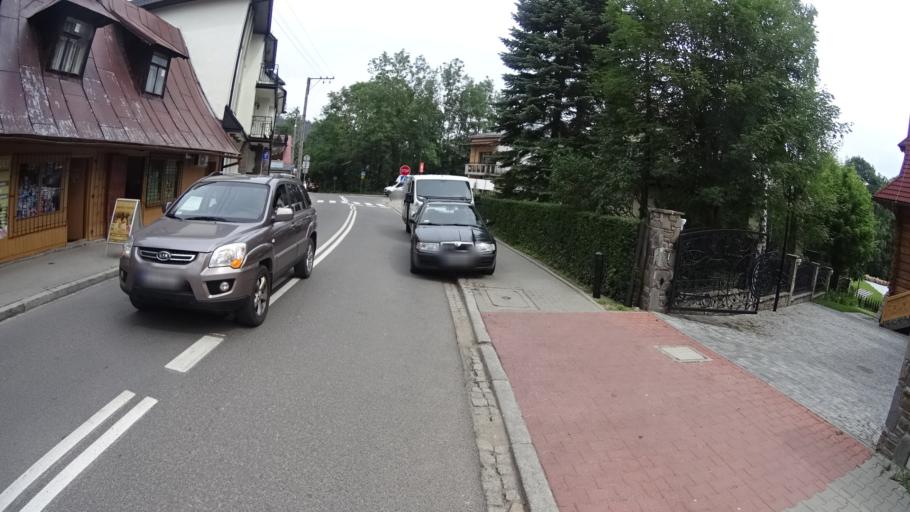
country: PL
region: Lesser Poland Voivodeship
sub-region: Powiat tatrzanski
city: Zakopane
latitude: 49.2912
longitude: 19.9481
